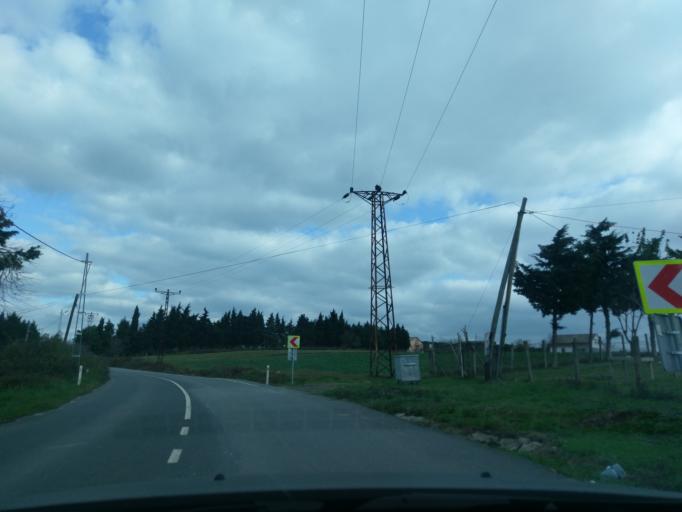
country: TR
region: Istanbul
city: Durusu
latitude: 41.3263
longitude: 28.6753
